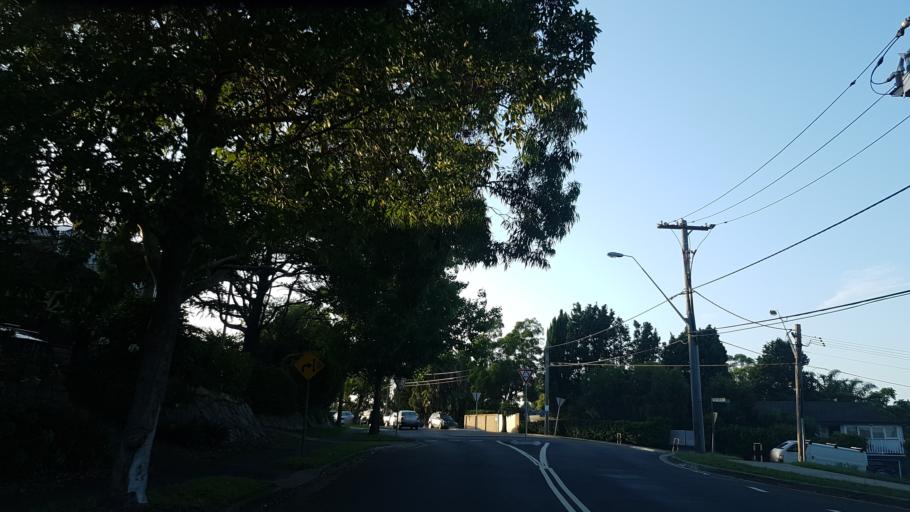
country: AU
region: New South Wales
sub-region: Warringah
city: Narraweena
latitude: -33.7320
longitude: 151.2773
